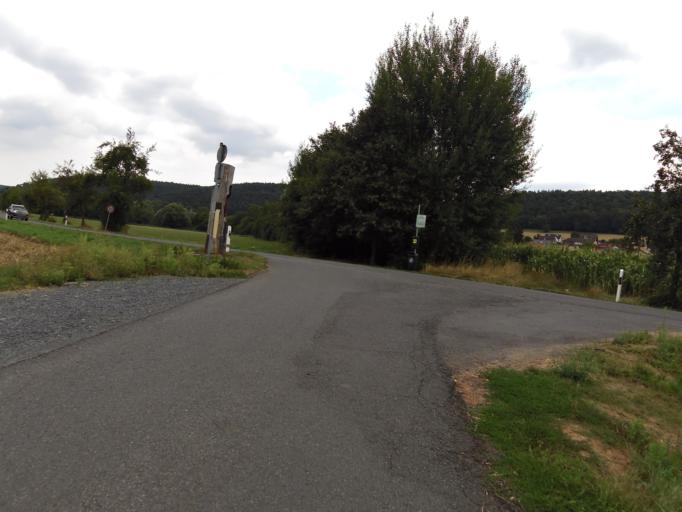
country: DE
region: Hesse
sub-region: Regierungsbezirk Darmstadt
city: Lutzelbach
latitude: 49.8156
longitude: 9.0492
